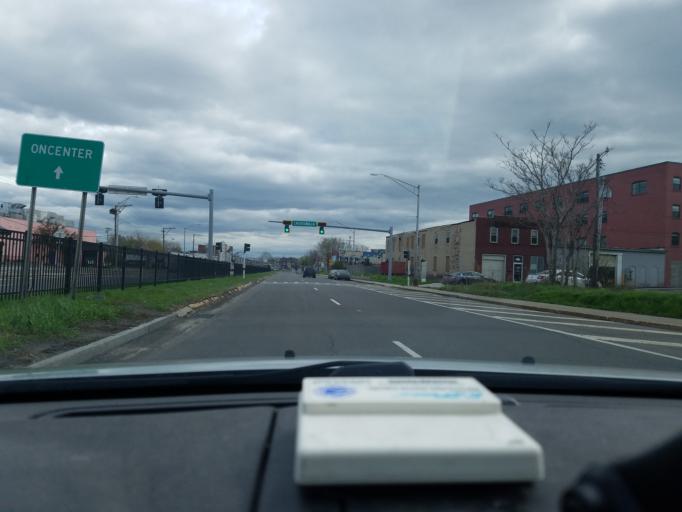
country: US
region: New York
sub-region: Onondaga County
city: Syracuse
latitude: 43.0471
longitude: -76.1588
